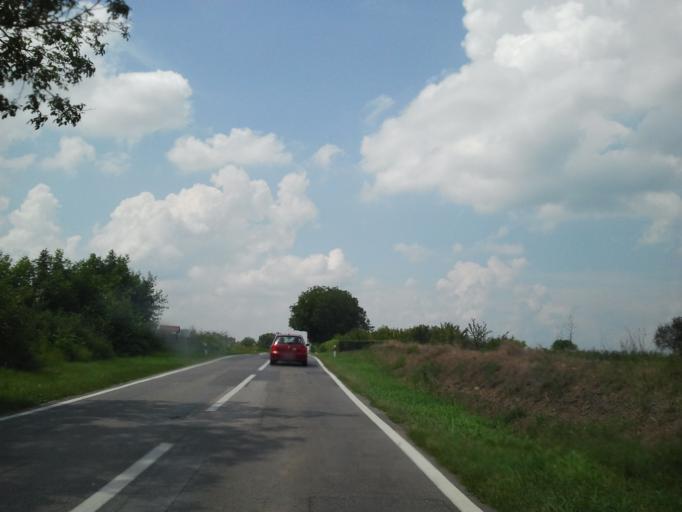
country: HR
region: Vukovarsko-Srijemska
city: Lovas
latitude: 45.2636
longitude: 19.1624
